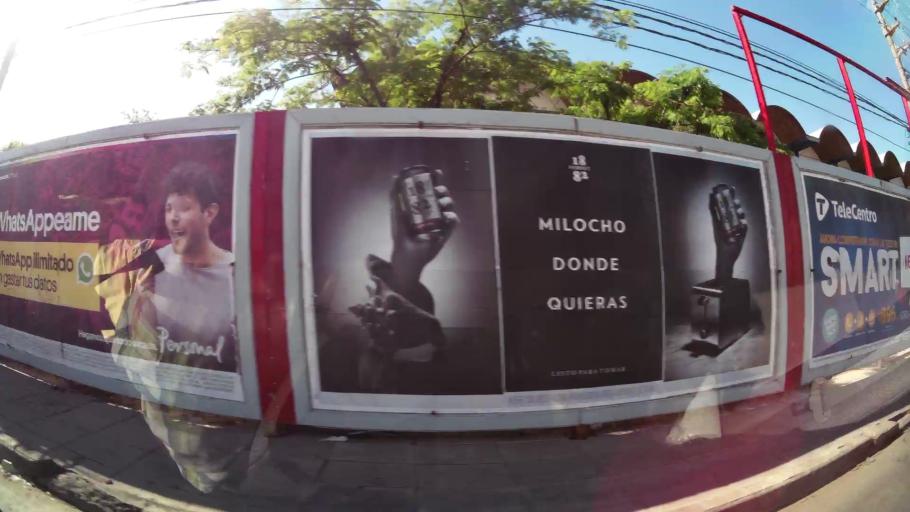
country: AR
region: Buenos Aires
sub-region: Partido de Tigre
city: Tigre
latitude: -34.4741
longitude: -58.5721
